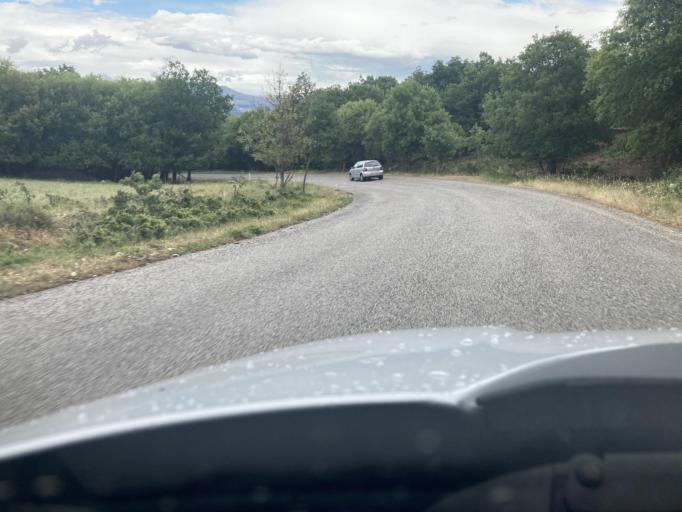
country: IT
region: Abruzzo
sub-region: Provincia dell' Aquila
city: San Panfilo d'Ocre
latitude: 42.2803
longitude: 13.4696
